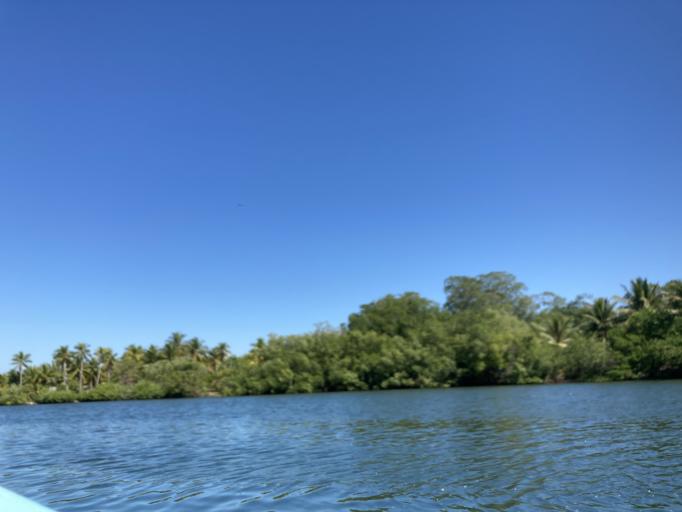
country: GT
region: Jutiapa
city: Pasaco
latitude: 13.8069
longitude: -90.2701
